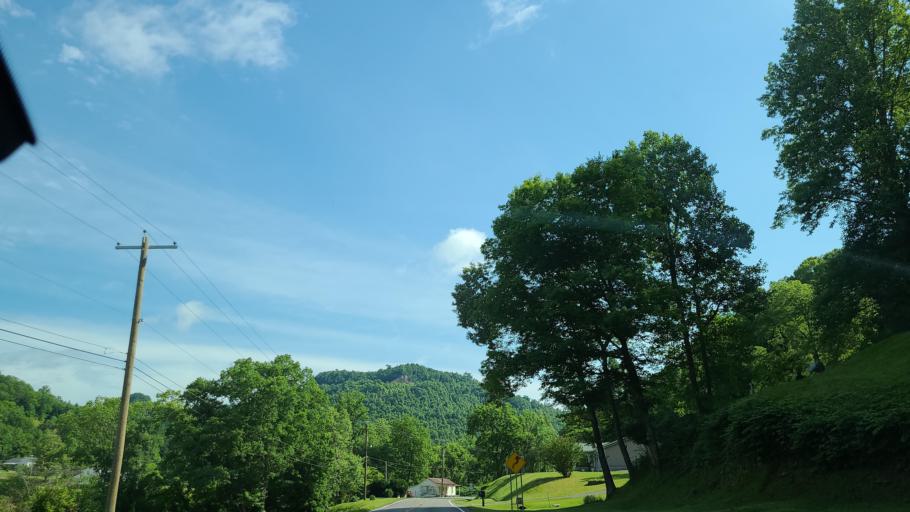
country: US
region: Kentucky
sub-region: Bell County
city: Pineville
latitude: 36.7799
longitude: -83.7706
